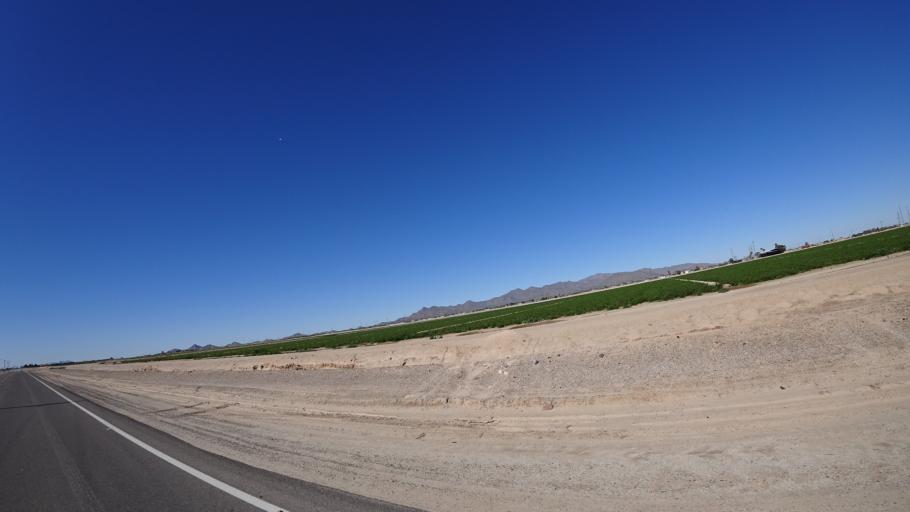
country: US
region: Arizona
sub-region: Maricopa County
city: Buckeye
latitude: 33.4068
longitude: -112.5241
